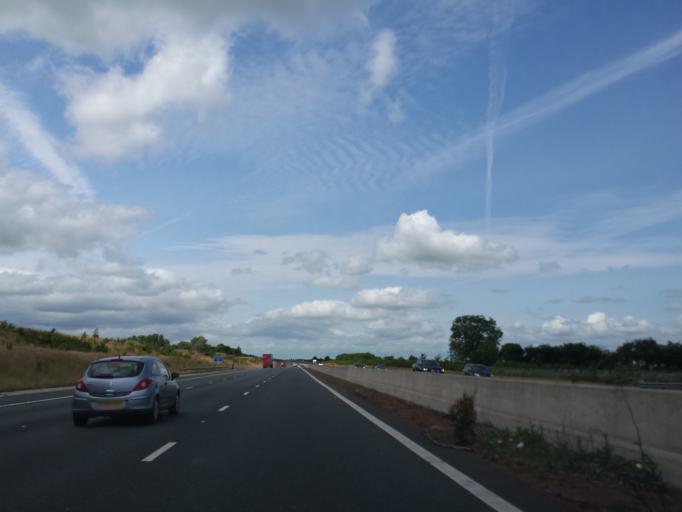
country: GB
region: England
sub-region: North Yorkshire
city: Bedale
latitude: 54.2501
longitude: -1.5071
